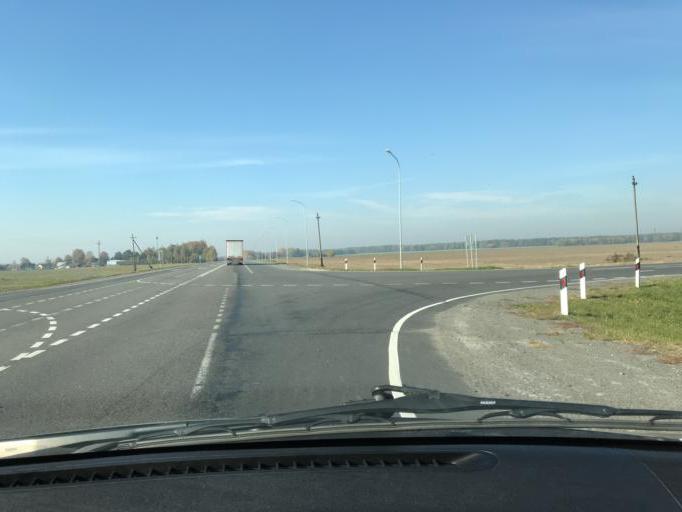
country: BY
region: Brest
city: Horad Luninyets
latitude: 52.3167
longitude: 26.6290
